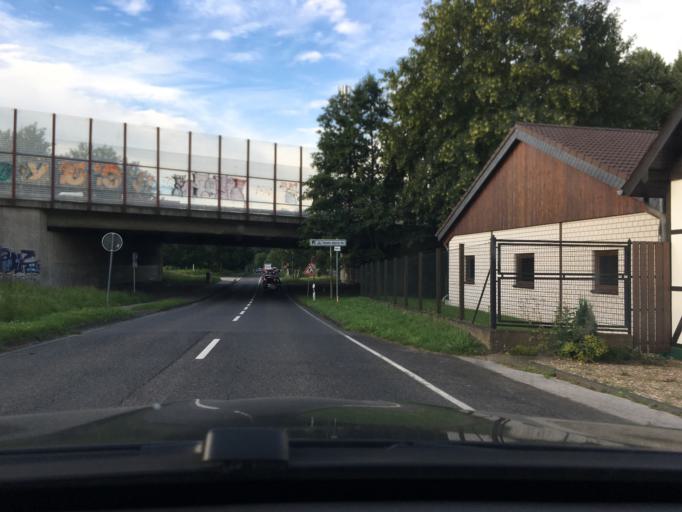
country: DE
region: North Rhine-Westphalia
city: Opladen
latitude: 51.0573
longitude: 7.0566
